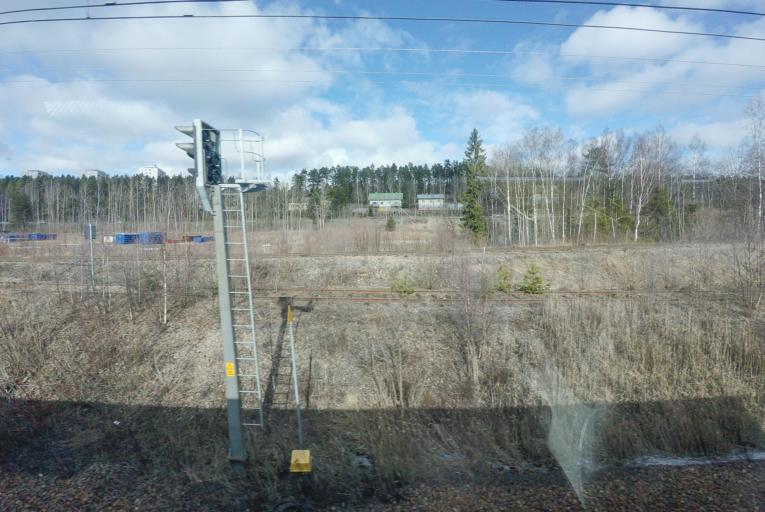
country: FI
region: Paijanne Tavastia
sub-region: Lahti
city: Lahti
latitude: 60.9725
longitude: 25.6952
